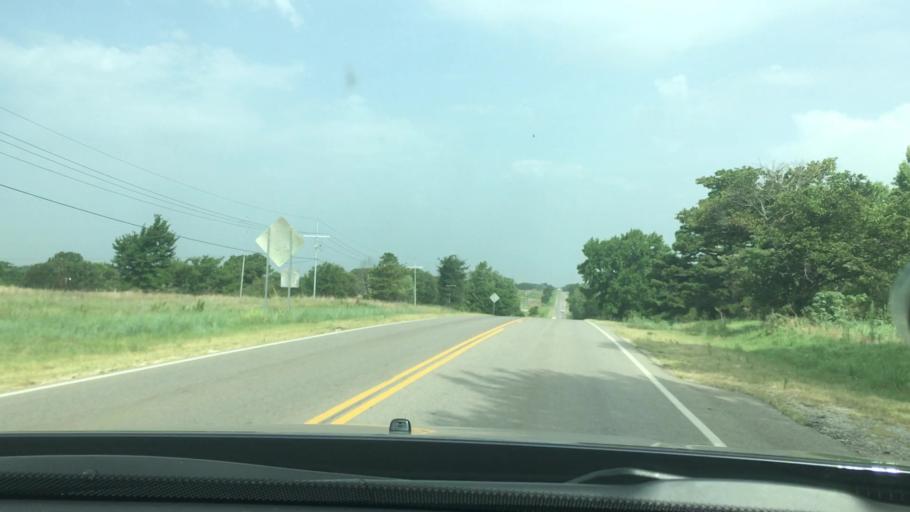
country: US
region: Oklahoma
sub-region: Pontotoc County
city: Ada
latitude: 34.7832
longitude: -96.7861
